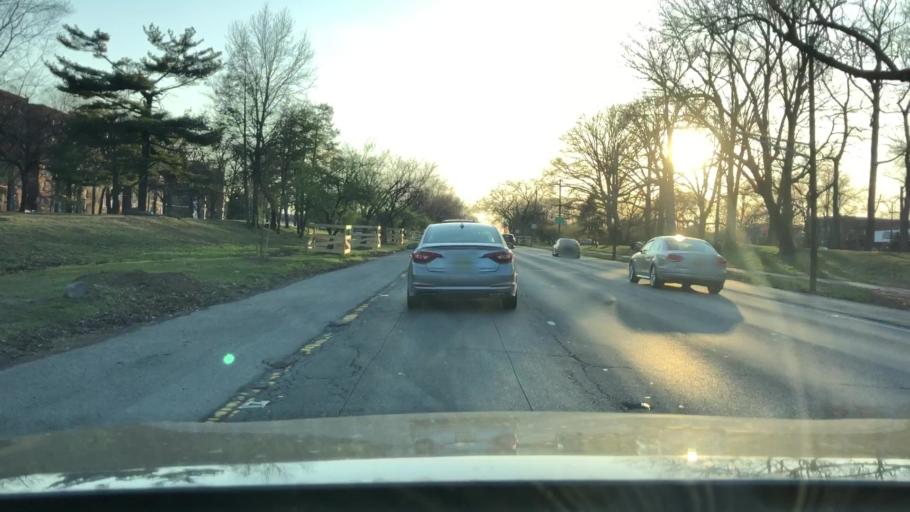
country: US
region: New York
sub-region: Bronx
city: The Bronx
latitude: 40.8577
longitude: -73.8534
